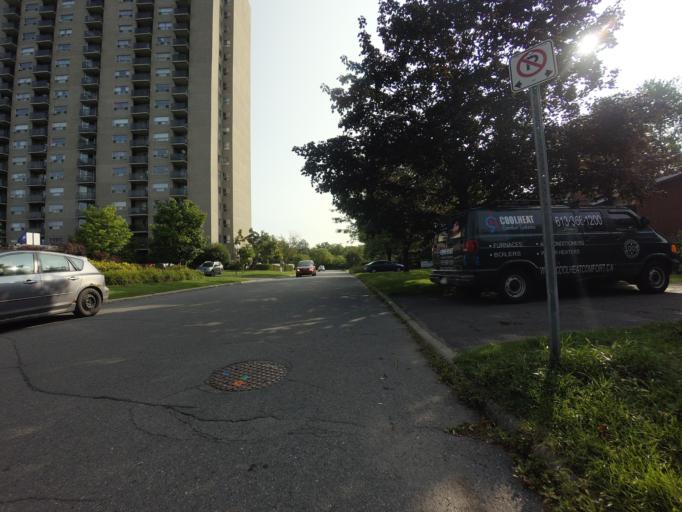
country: CA
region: Ontario
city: Ottawa
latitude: 45.3687
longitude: -75.7458
